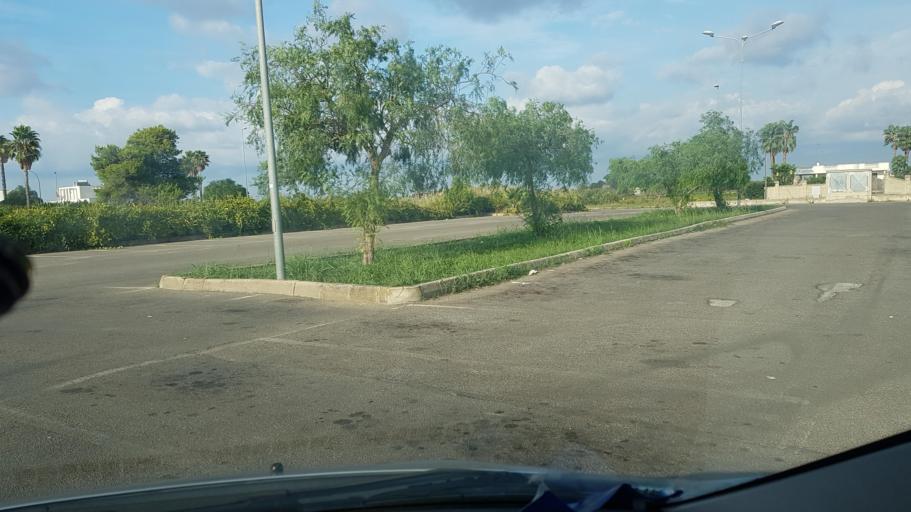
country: IT
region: Apulia
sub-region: Provincia di Lecce
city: Veglie
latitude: 40.3280
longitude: 17.9748
